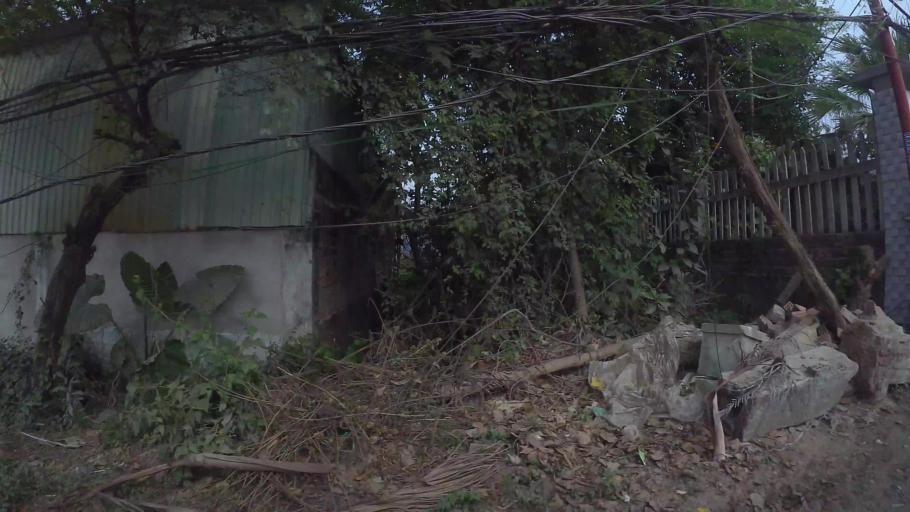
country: VN
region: Da Nang
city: Lien Chieu
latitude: 16.0464
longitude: 108.1463
